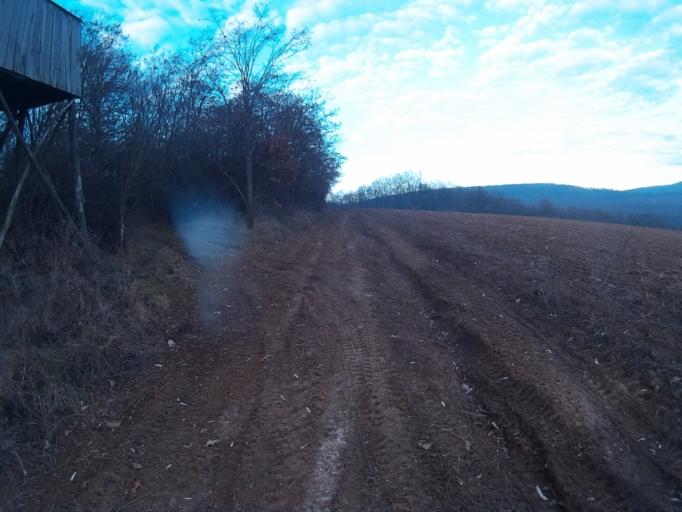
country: HU
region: Nograd
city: Rimoc
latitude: 47.9942
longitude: 19.4303
